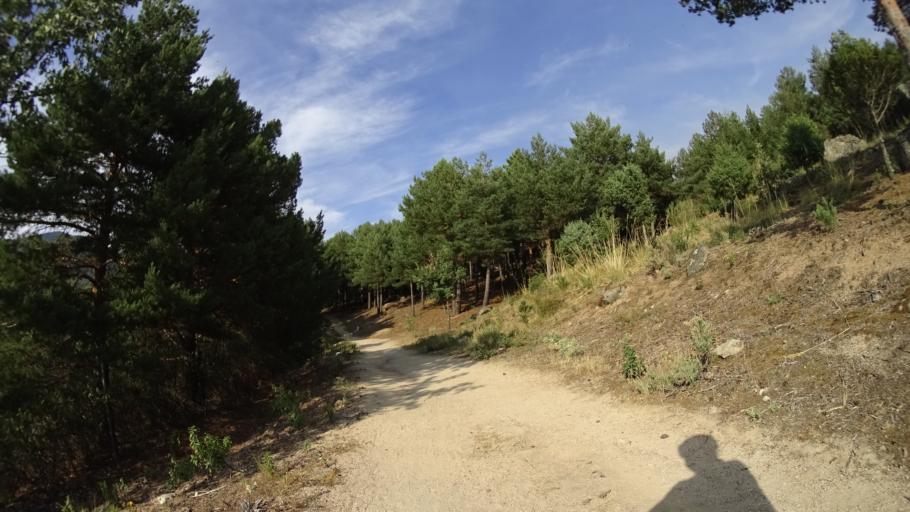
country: ES
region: Madrid
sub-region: Provincia de Madrid
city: Becerril de la Sierra
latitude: 40.7210
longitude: -4.0021
